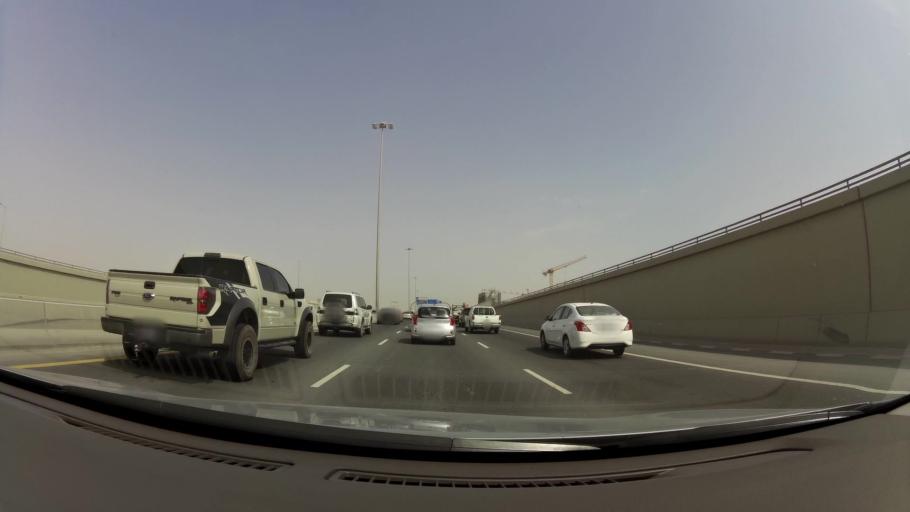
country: QA
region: Baladiyat ar Rayyan
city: Ar Rayyan
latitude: 25.2981
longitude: 51.4747
